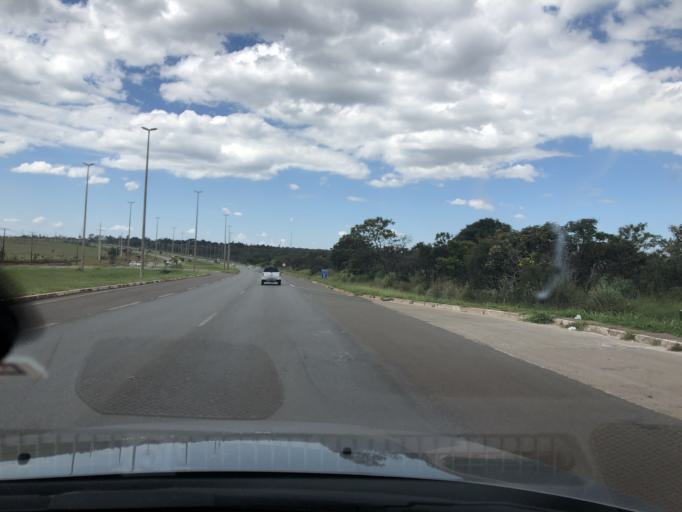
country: BR
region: Federal District
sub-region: Brasilia
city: Brasilia
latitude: -15.9758
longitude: -48.0103
